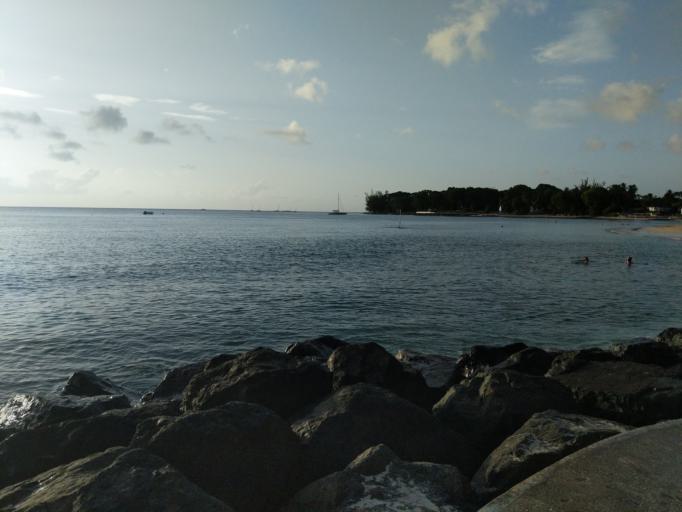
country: BB
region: Saint James
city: Holetown
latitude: 13.1857
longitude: -59.6387
